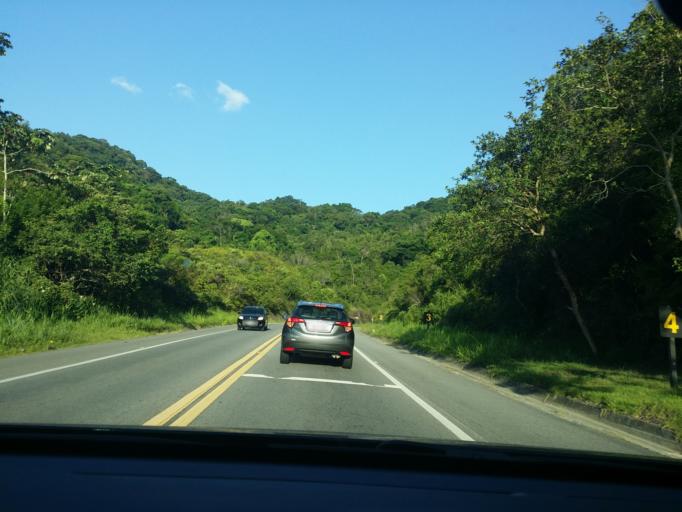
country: BR
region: Sao Paulo
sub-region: Sao Sebastiao
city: Sao Sebastiao
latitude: -23.7424
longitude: -45.7322
